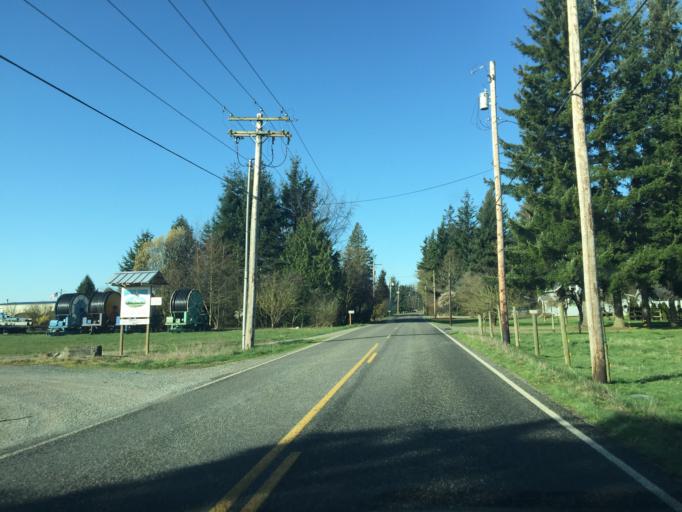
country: US
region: Washington
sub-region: Whatcom County
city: Lynden
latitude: 48.9064
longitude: -122.4981
